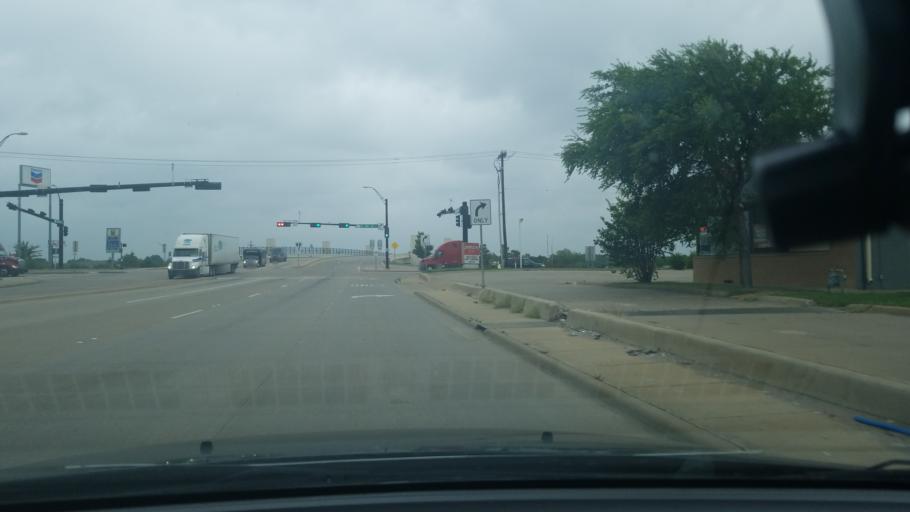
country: US
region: Texas
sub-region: Dallas County
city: Mesquite
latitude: 32.7915
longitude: -96.6557
